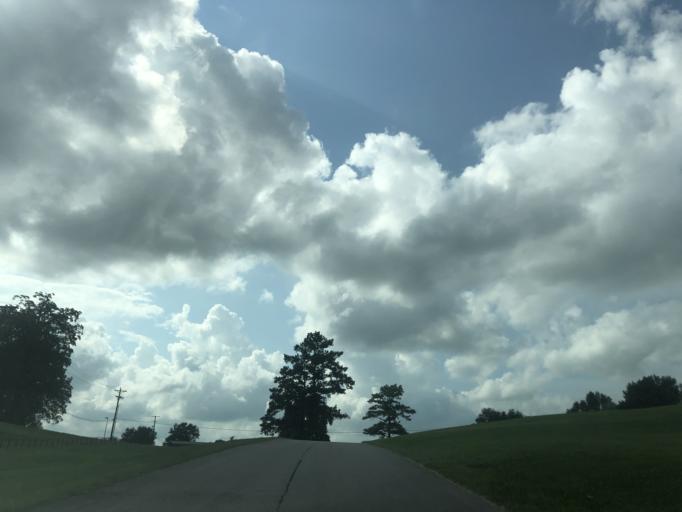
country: US
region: Tennessee
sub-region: Davidson County
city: Lakewood
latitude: 36.1628
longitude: -86.6426
